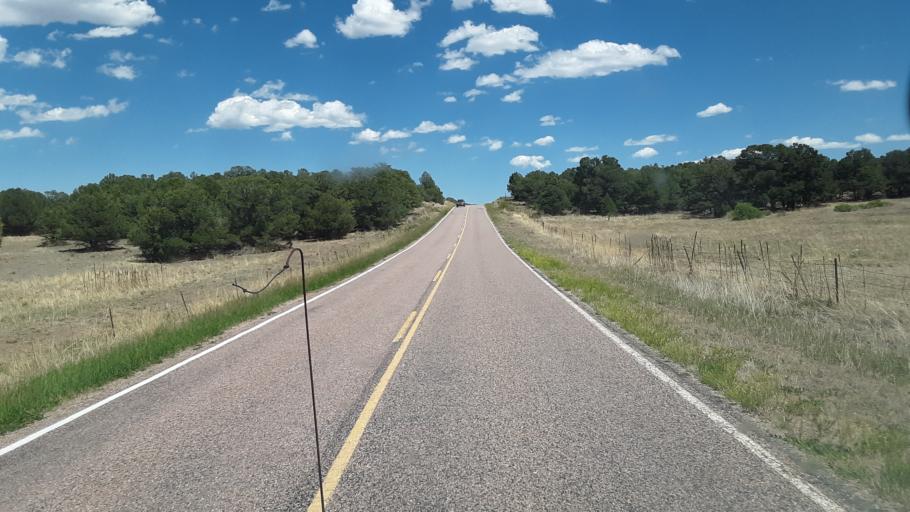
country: US
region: Colorado
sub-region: Custer County
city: Westcliffe
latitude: 38.3115
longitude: -105.6512
